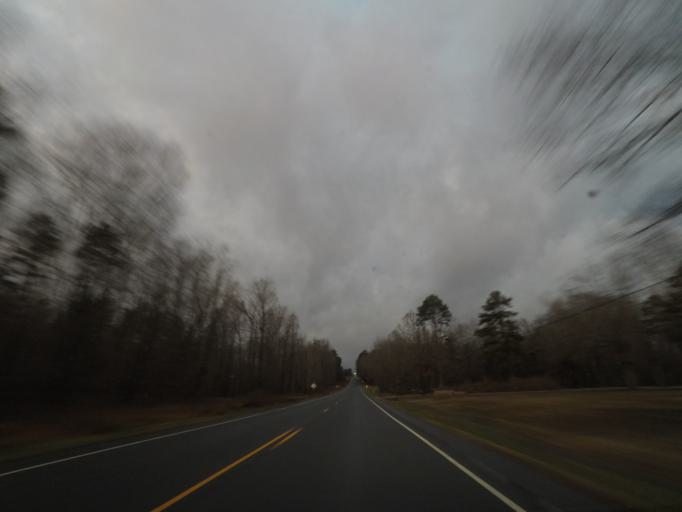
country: US
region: North Carolina
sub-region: Orange County
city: Hillsborough
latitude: 36.2051
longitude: -79.1520
